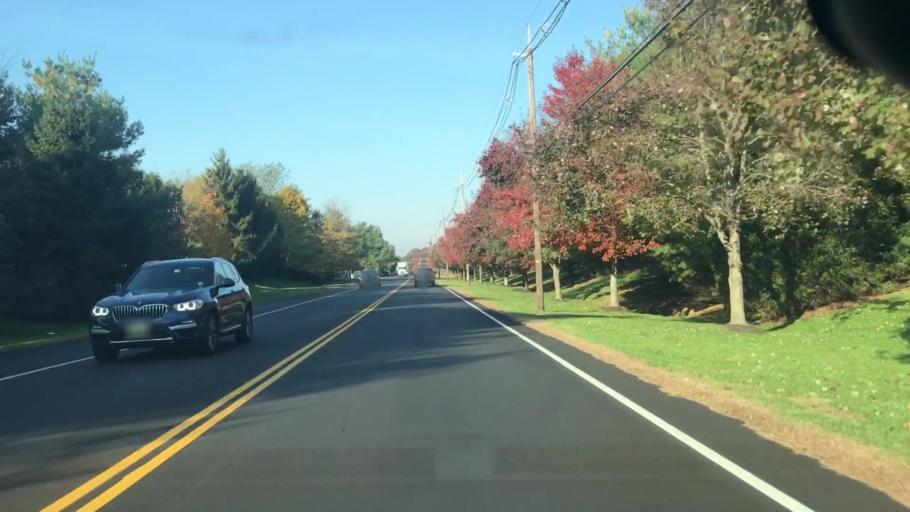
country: US
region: New Jersey
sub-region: Middlesex County
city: Princeton Meadows
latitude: 40.3367
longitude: -74.5528
